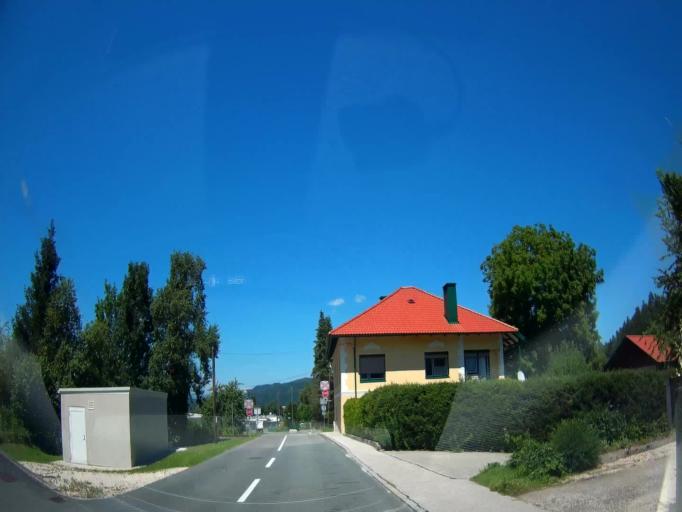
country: AT
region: Carinthia
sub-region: Politischer Bezirk Klagenfurt Land
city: Ferlach
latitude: 46.5199
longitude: 14.2977
